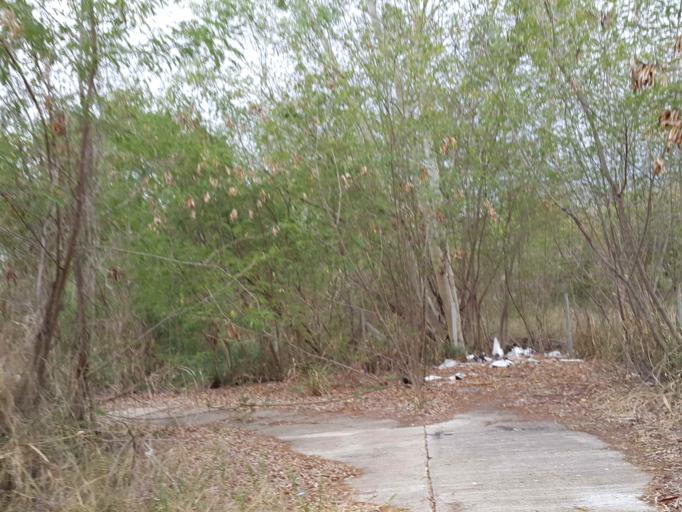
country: TH
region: Chiang Mai
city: Chiang Mai
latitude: 18.7626
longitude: 99.0217
